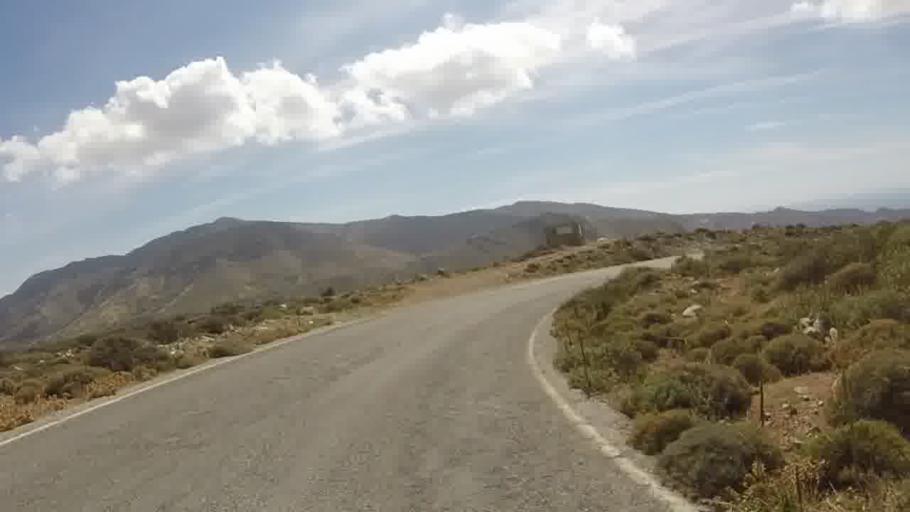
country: GR
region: Crete
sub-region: Nomos Rethymnis
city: Agia Galini
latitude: 35.1533
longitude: 24.6236
